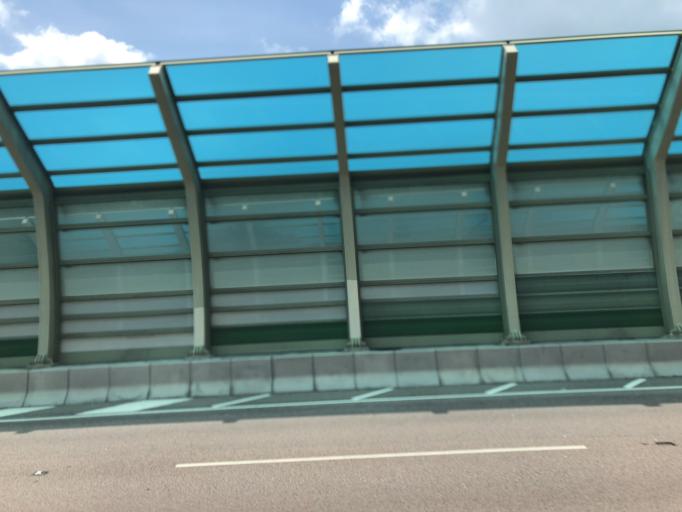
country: HK
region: Tsuen Wan
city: Tsuen Wan
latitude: 22.3634
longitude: 114.0403
